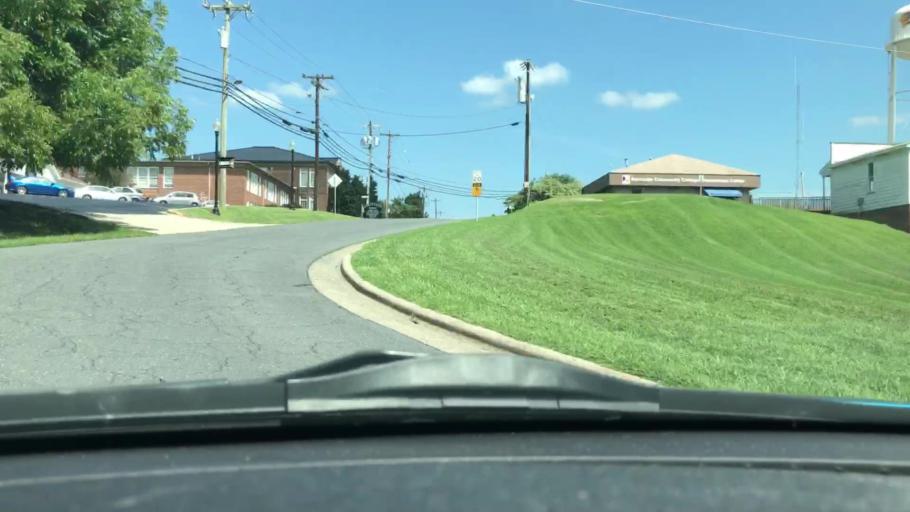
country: US
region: North Carolina
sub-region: Randolph County
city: Randleman
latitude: 35.8179
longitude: -79.8067
